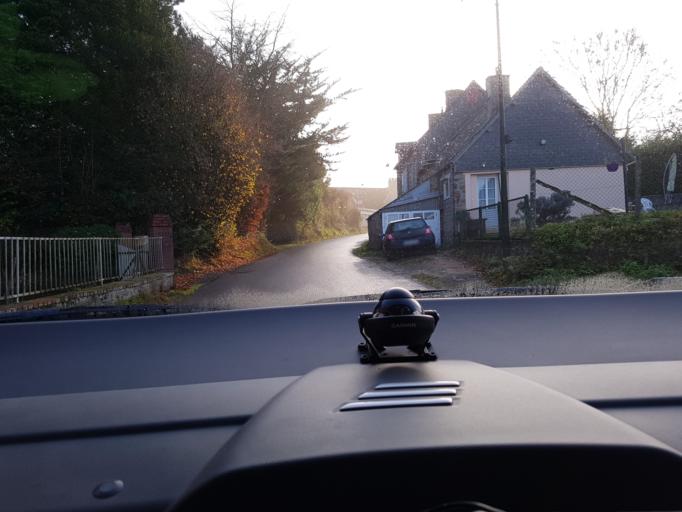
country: FR
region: Lower Normandy
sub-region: Departement de l'Orne
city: Champsecret
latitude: 48.6336
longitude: -0.5539
